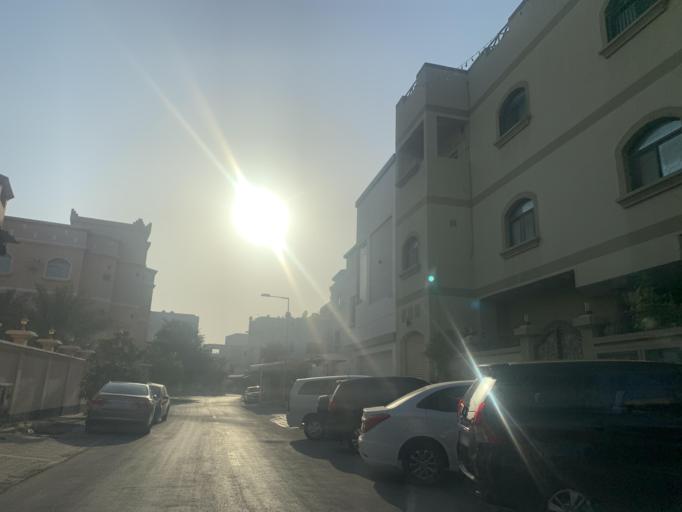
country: BH
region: Manama
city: Jidd Hafs
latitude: 26.2165
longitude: 50.5258
